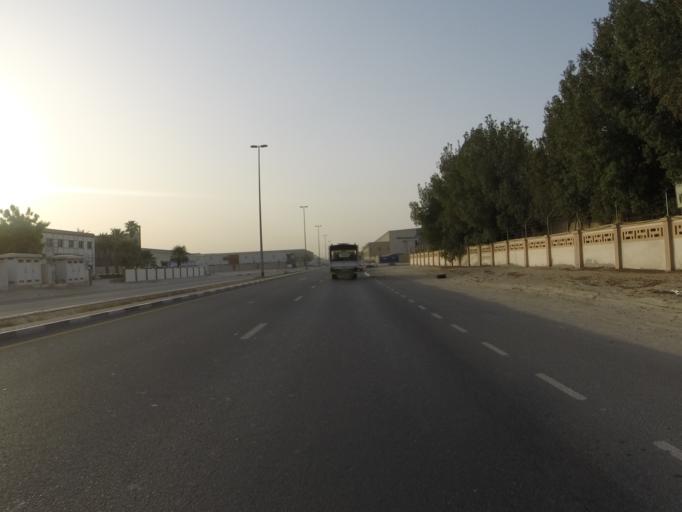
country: AE
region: Dubai
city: Dubai
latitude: 25.1349
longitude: 55.2249
